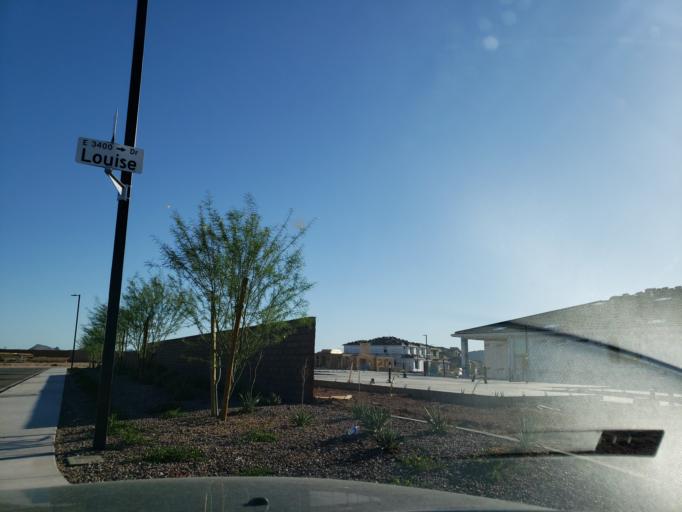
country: US
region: Arizona
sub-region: Maricopa County
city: Cave Creek
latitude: 33.6855
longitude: -112.0081
